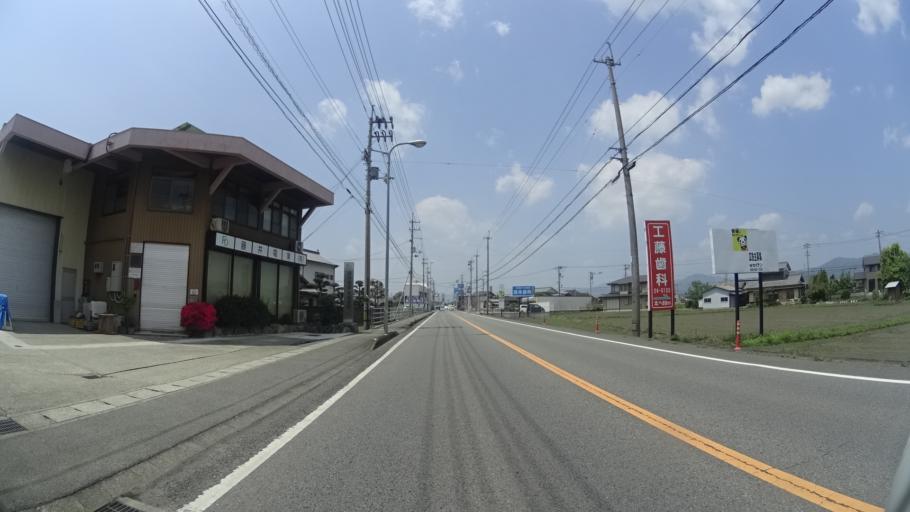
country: JP
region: Tokushima
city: Kamojimacho-jogejima
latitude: 34.0691
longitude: 134.3392
